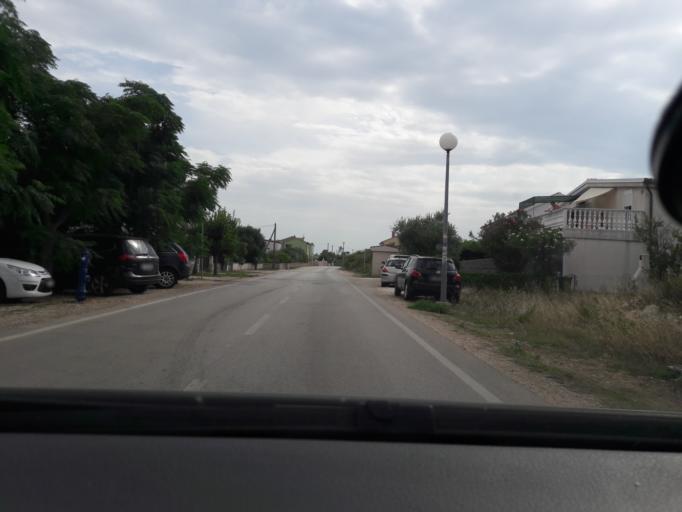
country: HR
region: Zadarska
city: Vir
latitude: 44.2989
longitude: 15.0779
